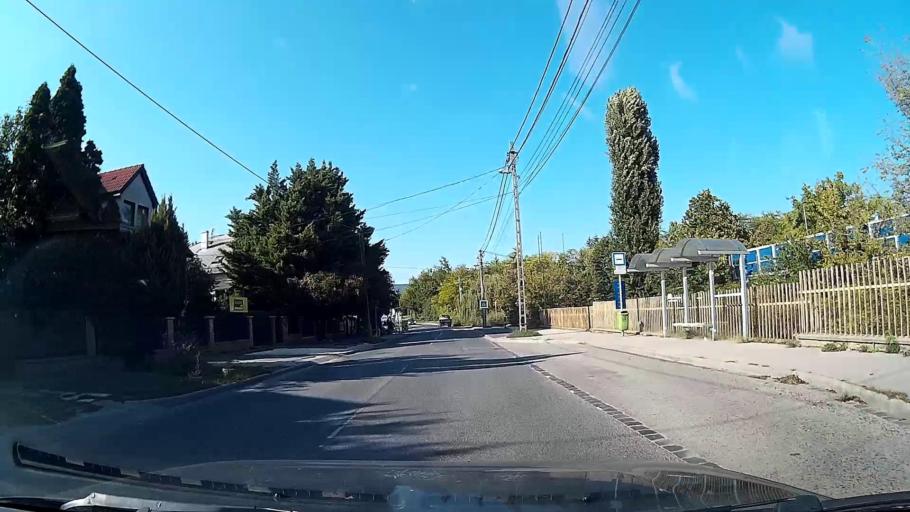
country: HU
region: Pest
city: Budaors
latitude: 47.4406
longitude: 18.9793
